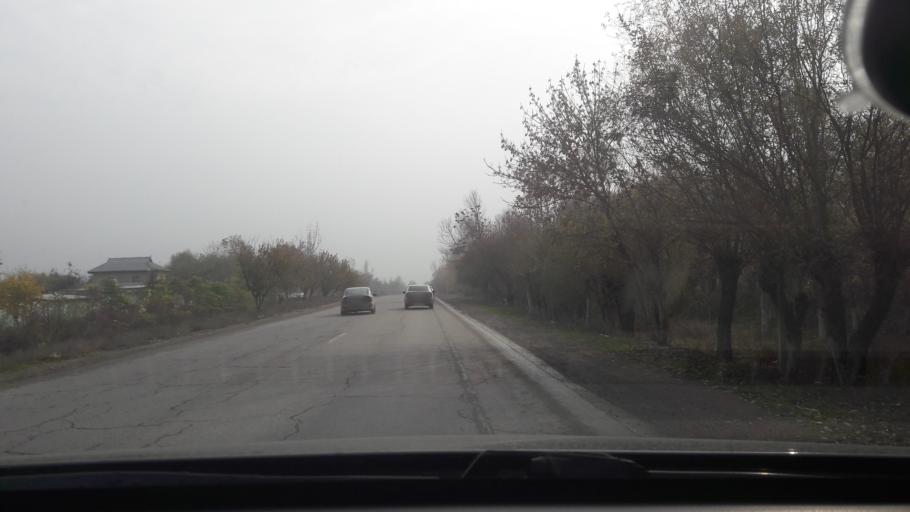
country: TJ
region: Khatlon
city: Qurghonteppa
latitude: 37.8751
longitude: 68.6972
